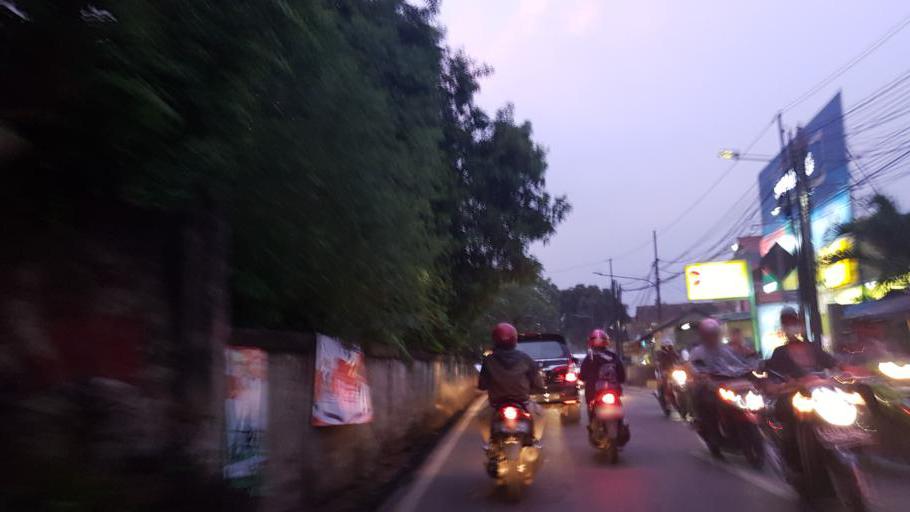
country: ID
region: West Java
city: Depok
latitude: -6.3519
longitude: 106.8015
